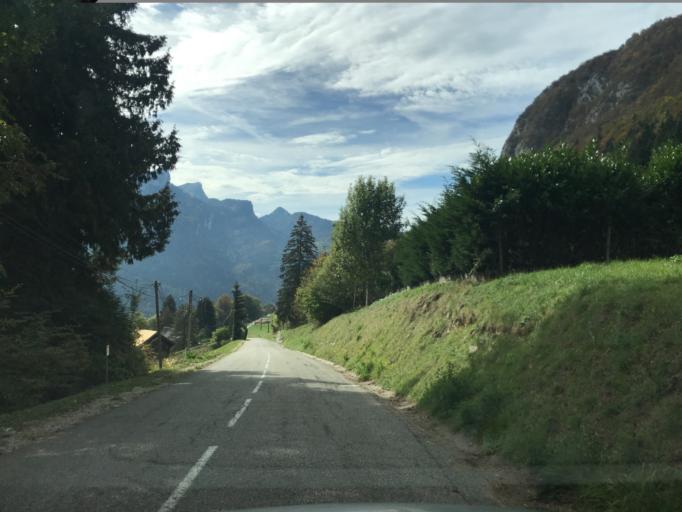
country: FR
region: Rhone-Alpes
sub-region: Departement de la Savoie
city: Les Echelles
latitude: 45.4375
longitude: 5.8312
